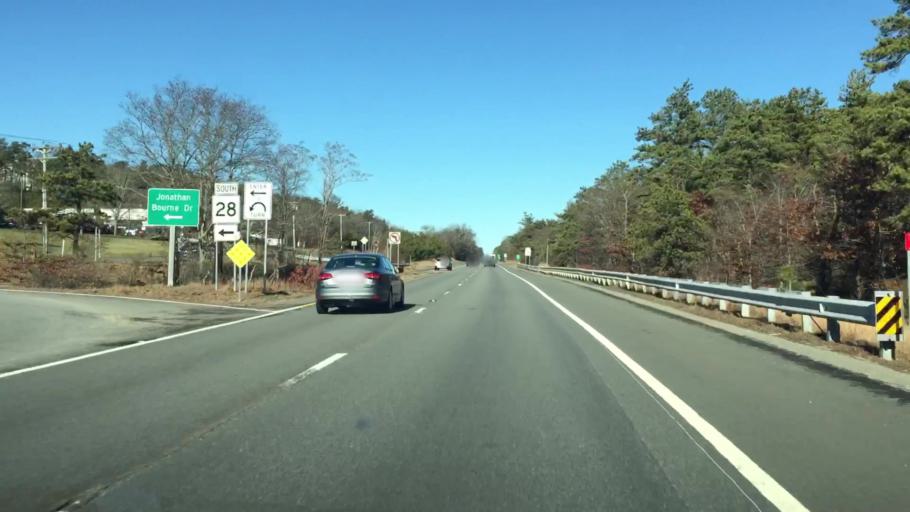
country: US
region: Massachusetts
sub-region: Barnstable County
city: Monument Beach
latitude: 41.7114
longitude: -70.5829
